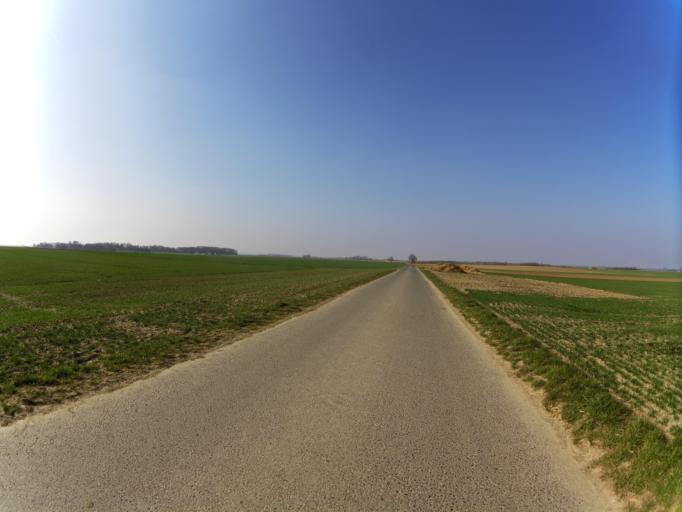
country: DE
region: Bavaria
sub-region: Regierungsbezirk Unterfranken
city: Gaukonigshofen
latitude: 49.6509
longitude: 9.9990
